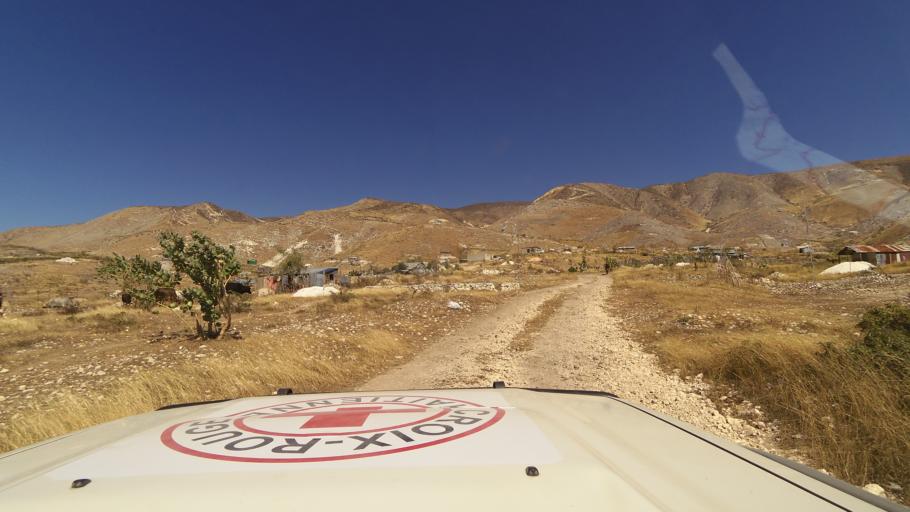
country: HT
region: Ouest
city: Croix des Bouquets
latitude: 18.6752
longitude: -72.2866
